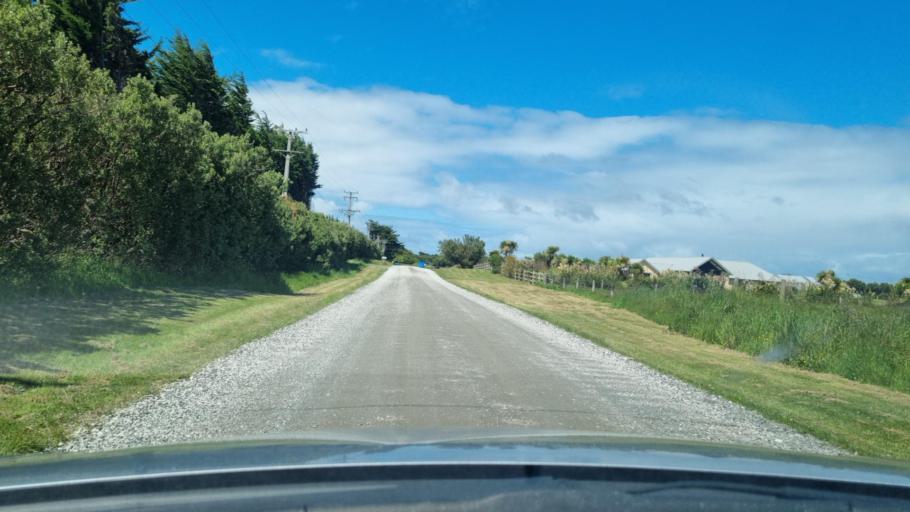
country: NZ
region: Southland
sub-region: Invercargill City
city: Invercargill
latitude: -46.4424
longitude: 168.2784
